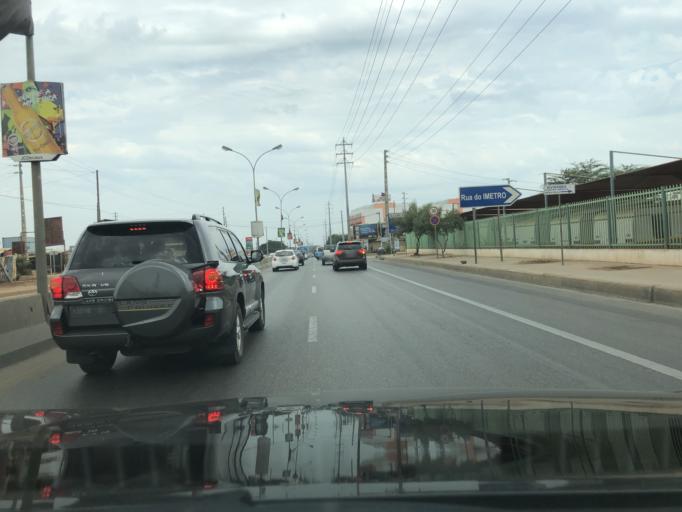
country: AO
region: Luanda
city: Luanda
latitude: -8.9011
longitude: 13.2044
